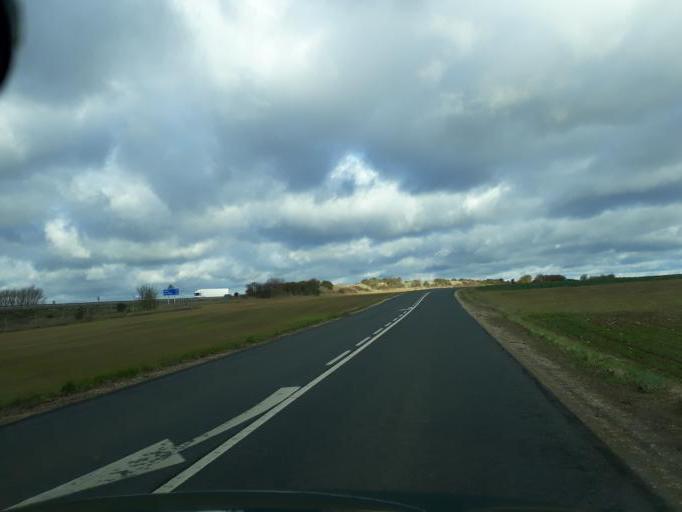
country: FR
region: Centre
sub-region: Departement du Loir-et-Cher
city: La Chaussee-Saint-Victor
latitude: 47.6323
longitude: 1.3571
